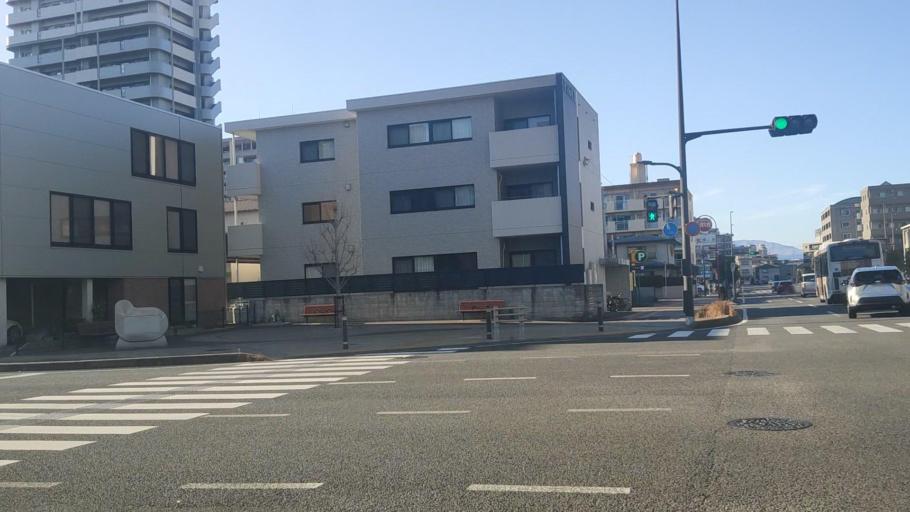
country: JP
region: Oita
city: Oita
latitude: 33.2328
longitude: 131.6035
